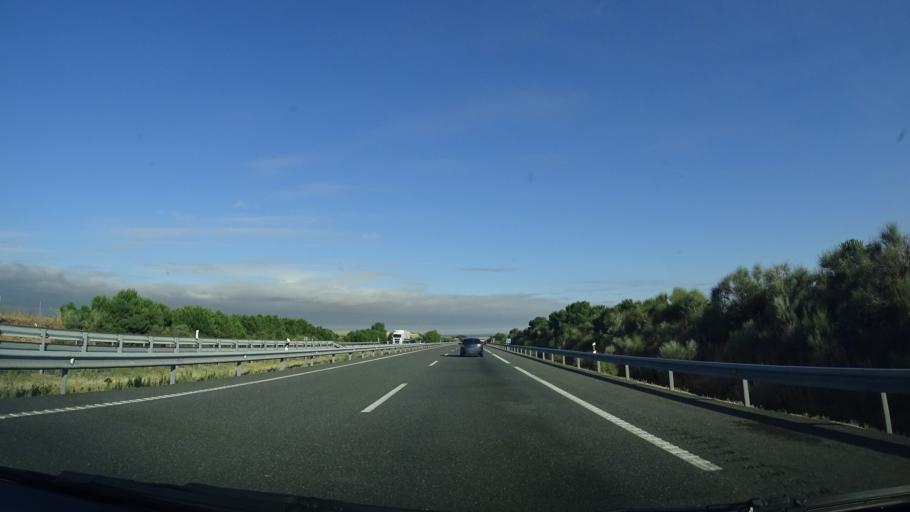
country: ES
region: Castille and Leon
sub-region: Provincia de Avila
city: Maello
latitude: 40.8249
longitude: -4.5151
